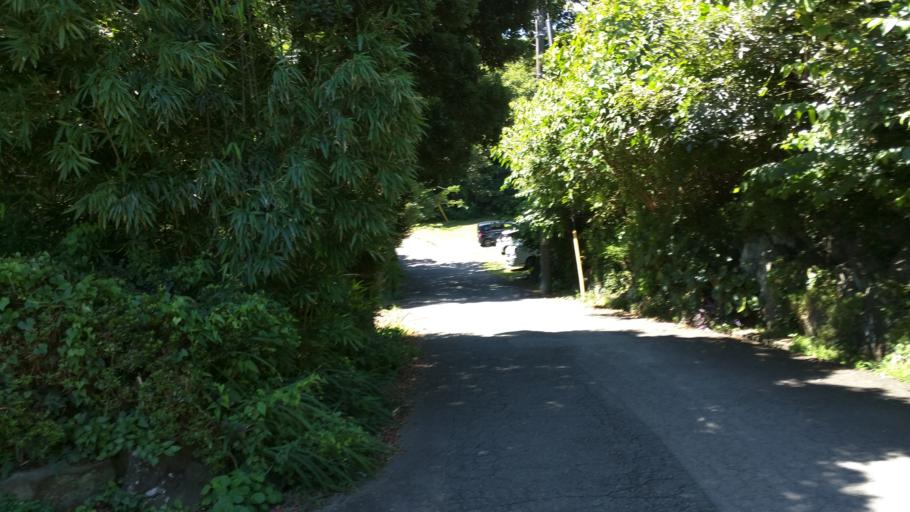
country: JP
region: Shizuoka
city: Ito
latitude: 34.8893
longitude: 139.1216
